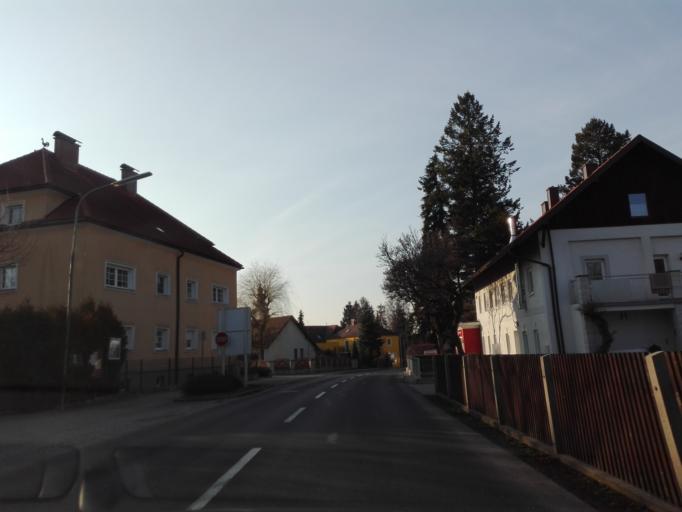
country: AT
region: Upper Austria
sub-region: Politischer Bezirk Linz-Land
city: Horsching
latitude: 48.2244
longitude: 14.1814
